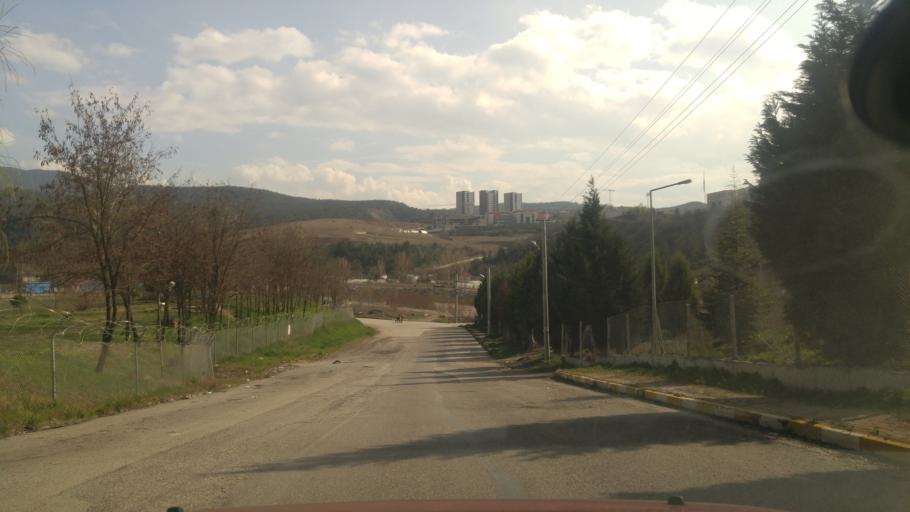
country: TR
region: Karabuk
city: Karabuk
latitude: 41.2153
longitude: 32.6581
